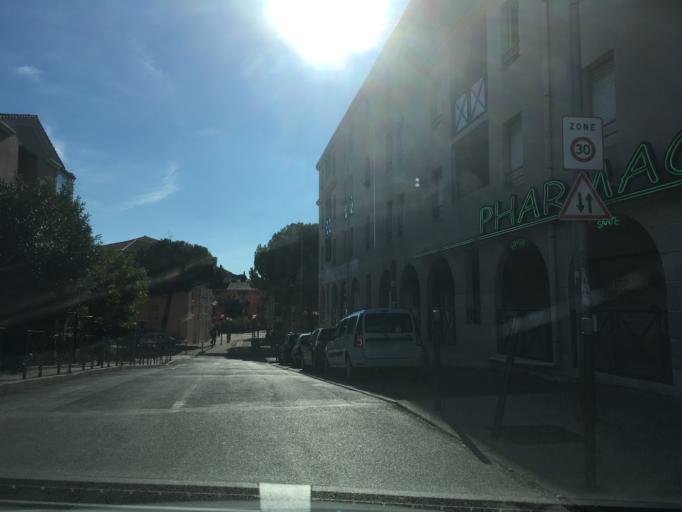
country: FR
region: Languedoc-Roussillon
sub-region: Departement de l'Herault
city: Juvignac
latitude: 43.6150
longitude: 3.8259
